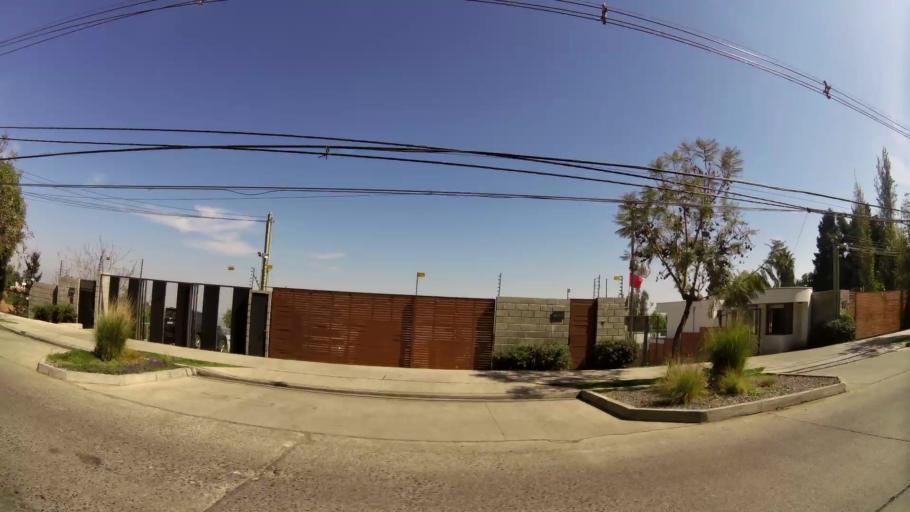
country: CL
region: Santiago Metropolitan
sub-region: Provincia de Santiago
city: Villa Presidente Frei, Nunoa, Santiago, Chile
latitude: -33.4564
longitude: -70.5209
